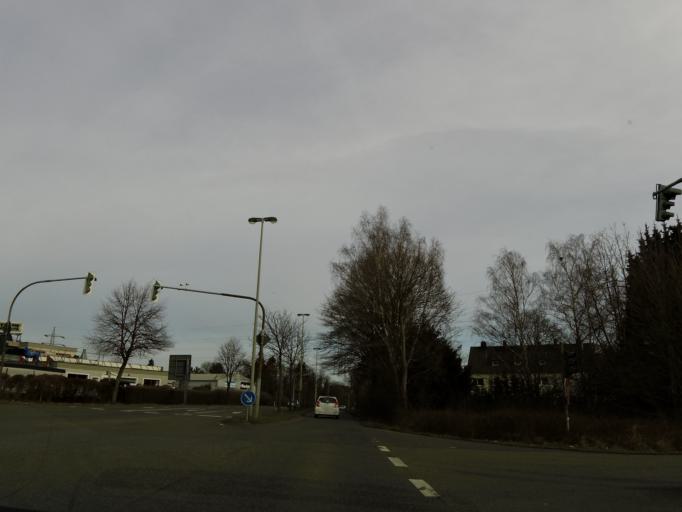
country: NL
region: Limburg
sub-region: Gemeente Kerkrade
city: Kerkrade
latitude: 50.8612
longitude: 6.0827
